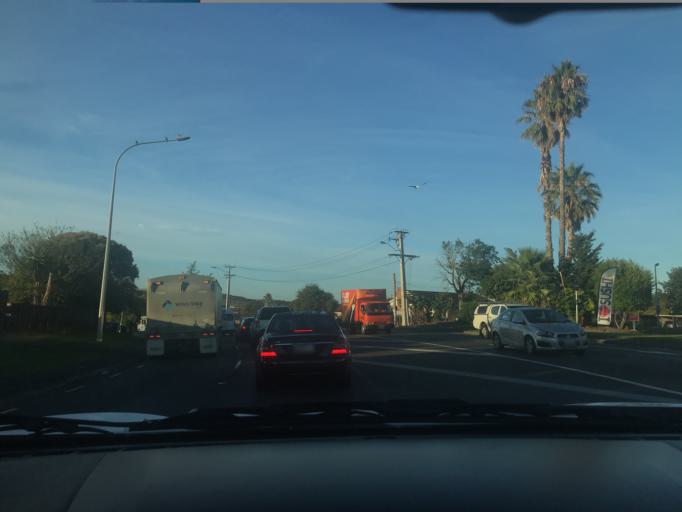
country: NZ
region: Auckland
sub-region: Auckland
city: Tamaki
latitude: -36.9099
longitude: 174.8379
